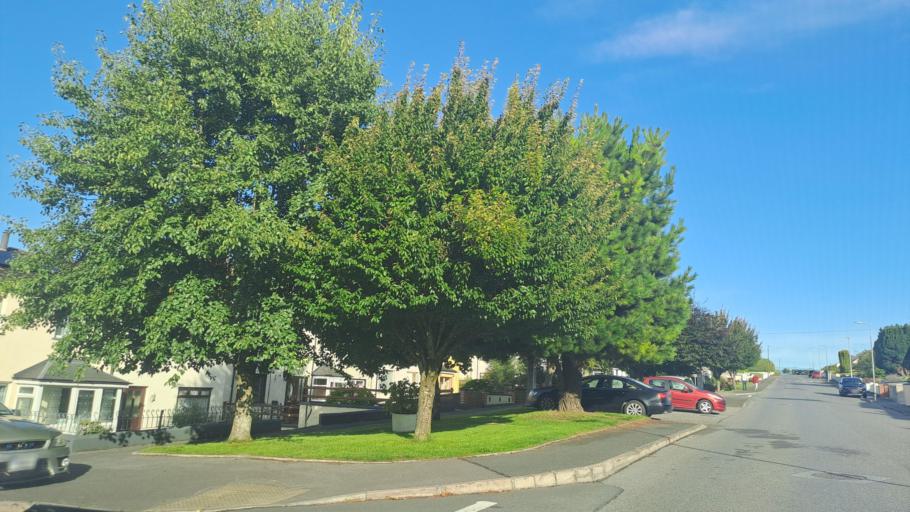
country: IE
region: Ulster
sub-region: County Monaghan
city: Carrickmacross
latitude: 53.9800
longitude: -6.7130
